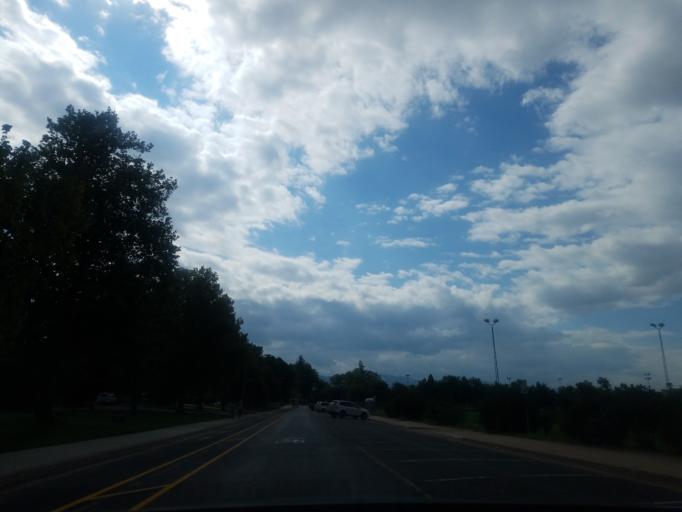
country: US
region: Colorado
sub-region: Larimer County
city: Fort Collins
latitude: 40.5726
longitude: -105.0930
